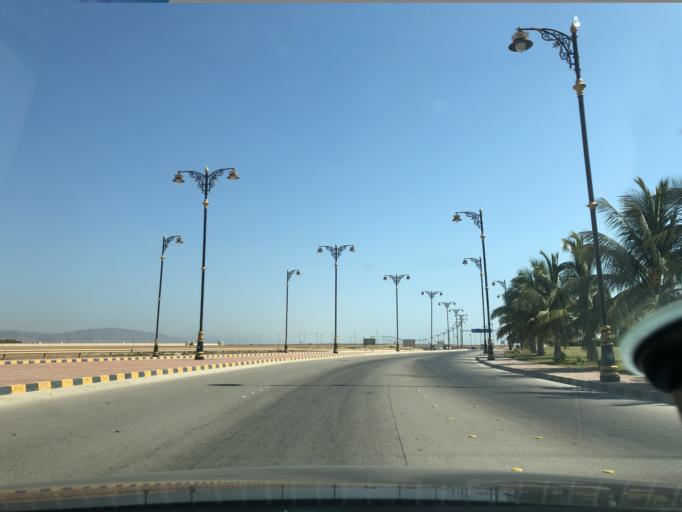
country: OM
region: Zufar
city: Salalah
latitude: 17.0513
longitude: 54.2192
